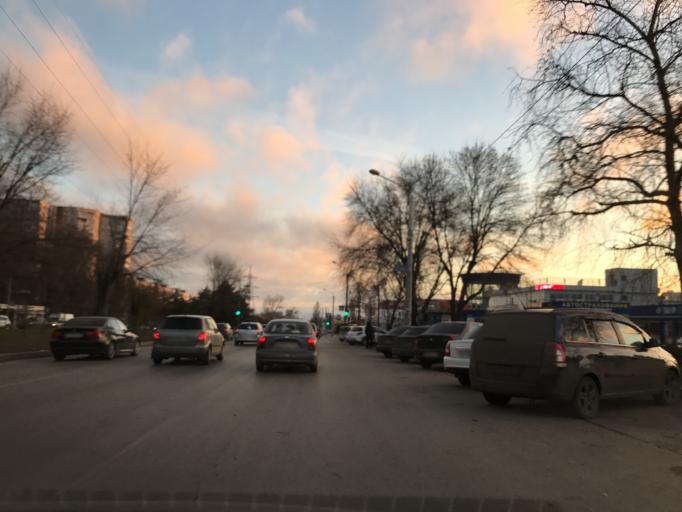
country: RU
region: Rostov
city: Kalinin
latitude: 47.2339
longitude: 39.6134
